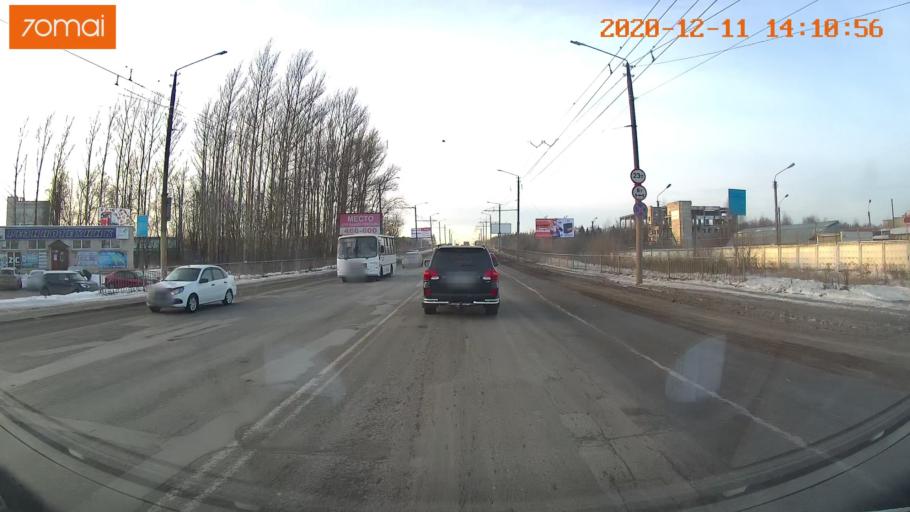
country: RU
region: Kostroma
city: Oktyabr'skiy
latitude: 57.7412
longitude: 40.9758
